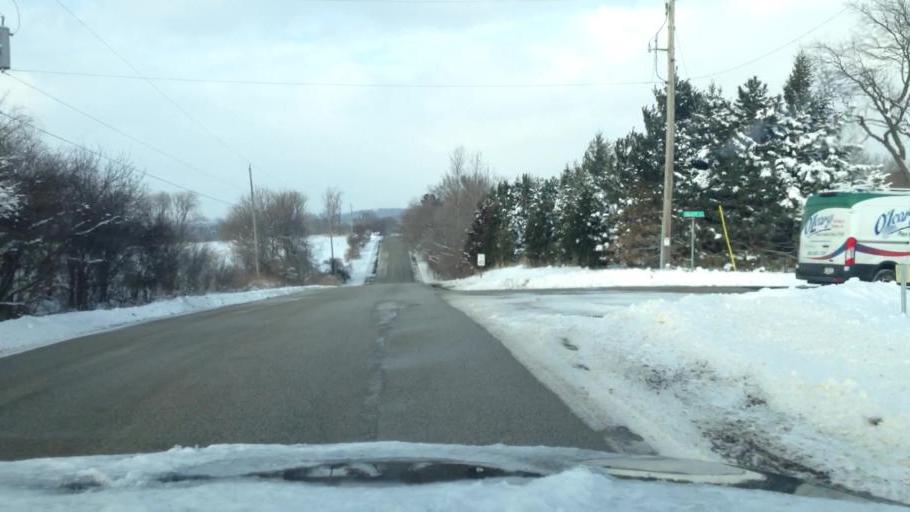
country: US
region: Wisconsin
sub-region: Walworth County
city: East Troy
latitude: 42.8227
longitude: -88.4244
